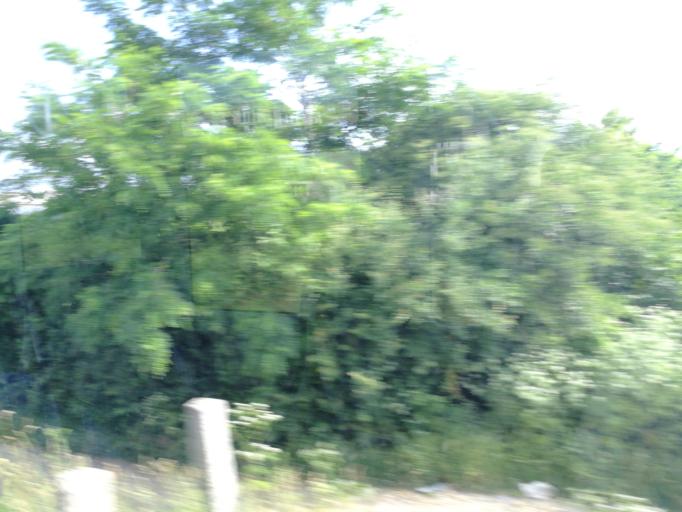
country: RO
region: Arges
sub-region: Comuna Bradu
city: Geamana
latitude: 44.8389
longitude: 24.9027
